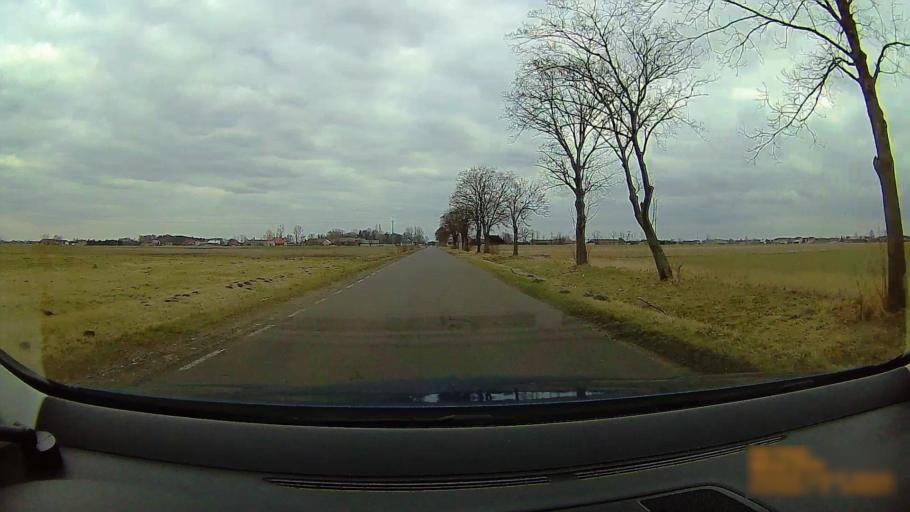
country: PL
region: Greater Poland Voivodeship
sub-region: Powiat koninski
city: Rychwal
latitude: 52.0967
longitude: 18.1319
